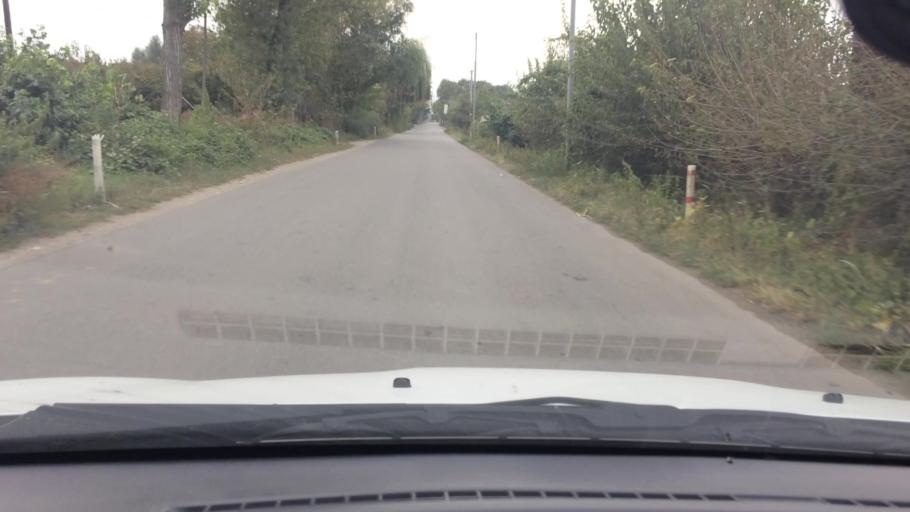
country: AM
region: Tavush
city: Bagratashen
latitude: 41.3332
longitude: 44.9120
